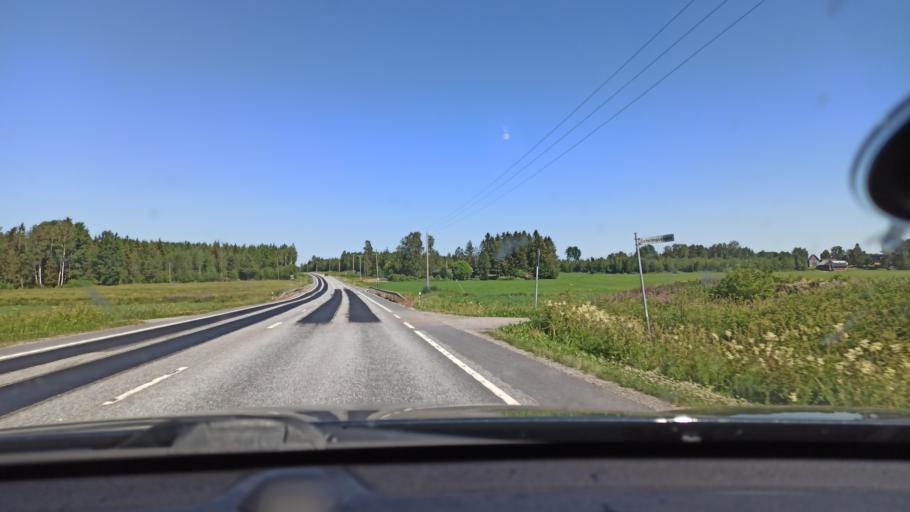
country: FI
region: Ostrobothnia
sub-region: Vaasa
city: Voera
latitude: 63.2143
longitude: 22.1990
